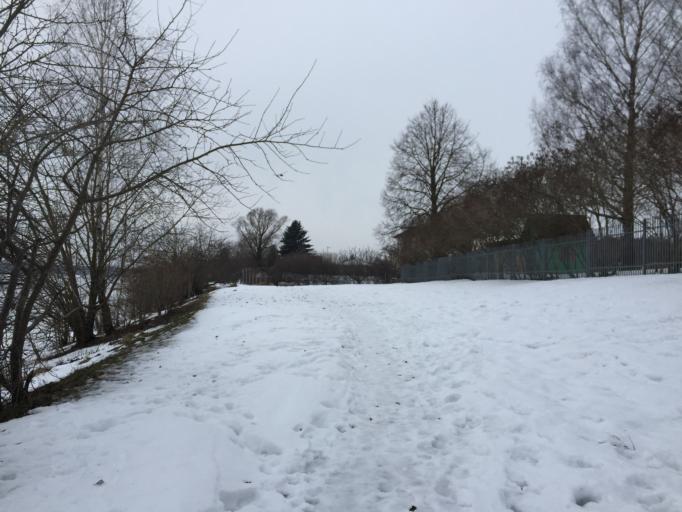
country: LV
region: Ikskile
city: Ikskile
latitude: 56.8434
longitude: 24.4366
